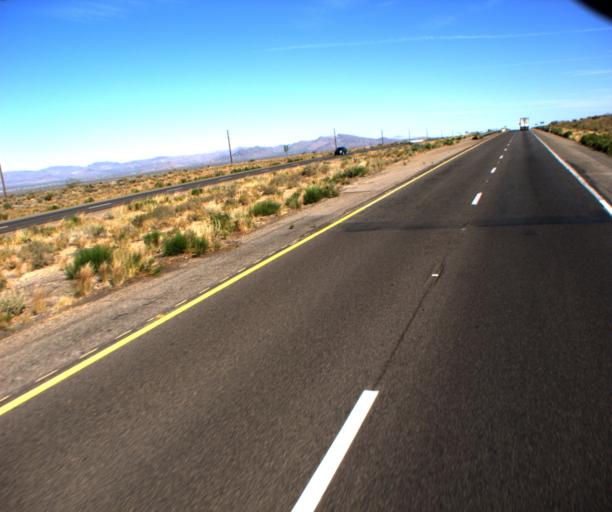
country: US
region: Arizona
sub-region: Mohave County
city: Golden Valley
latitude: 35.2466
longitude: -114.1502
